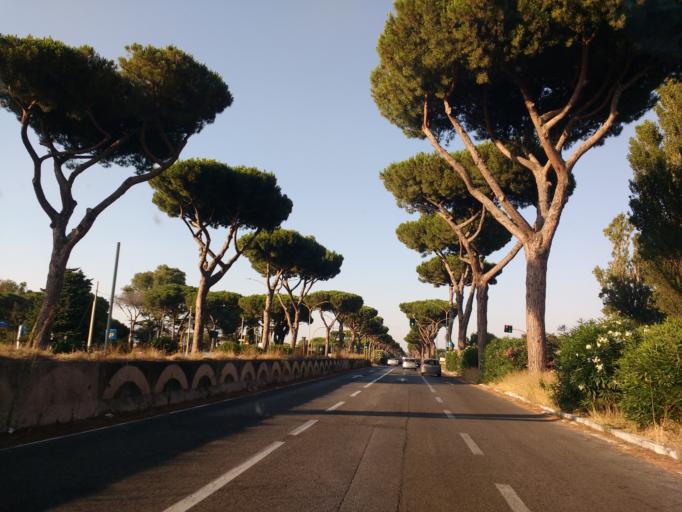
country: IT
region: Latium
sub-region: Citta metropolitana di Roma Capitale
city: Acilia-Castel Fusano-Ostia Antica
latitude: 41.7358
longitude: 12.3450
